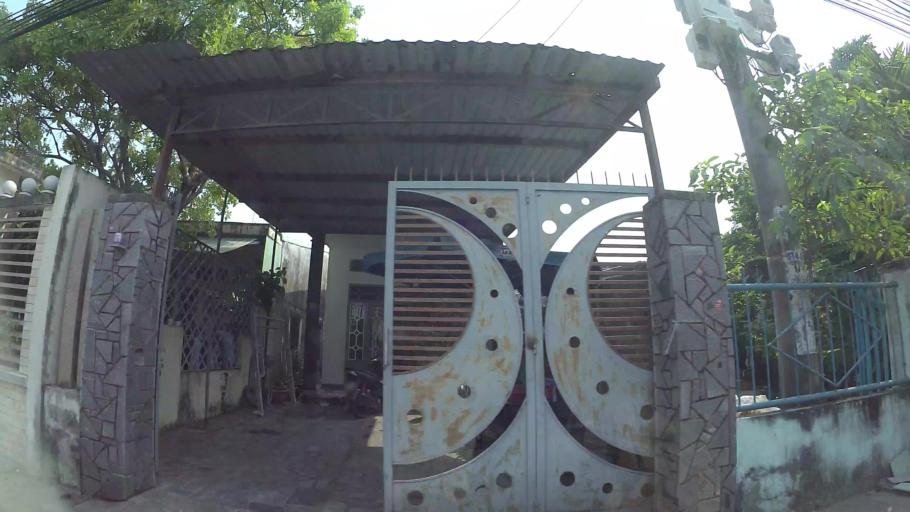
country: VN
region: Da Nang
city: Ngu Hanh Son
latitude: 15.9878
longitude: 108.2410
